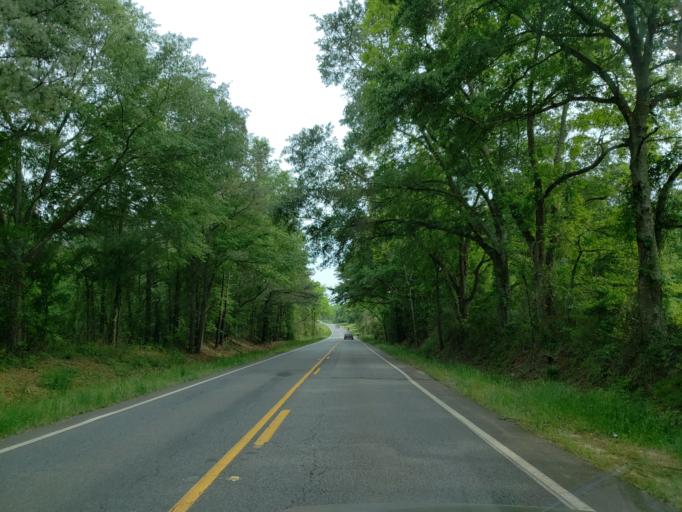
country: US
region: Georgia
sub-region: Macon County
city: Marshallville
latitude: 32.3998
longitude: -83.8663
